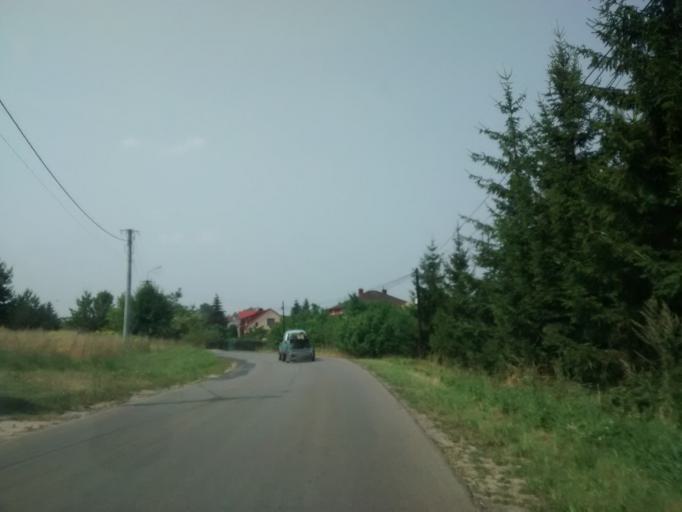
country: PL
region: Lesser Poland Voivodeship
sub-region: Powiat olkuski
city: Klucze
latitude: 50.3660
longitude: 19.5382
